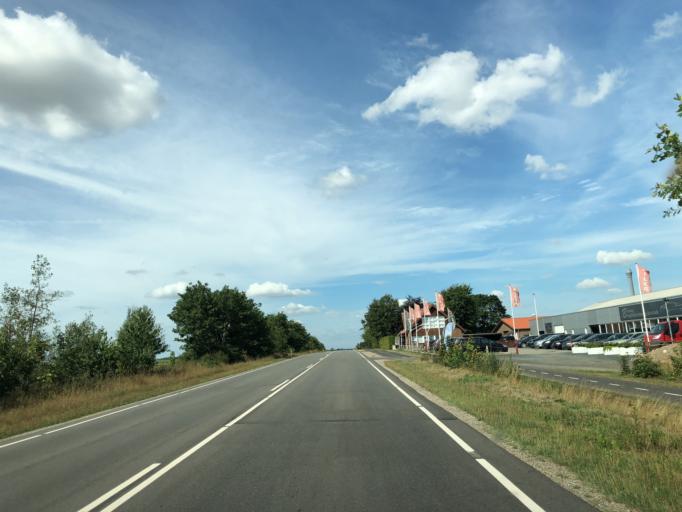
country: DK
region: Central Jutland
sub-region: Ikast-Brande Kommune
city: Bording Kirkeby
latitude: 56.1422
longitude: 9.2479
